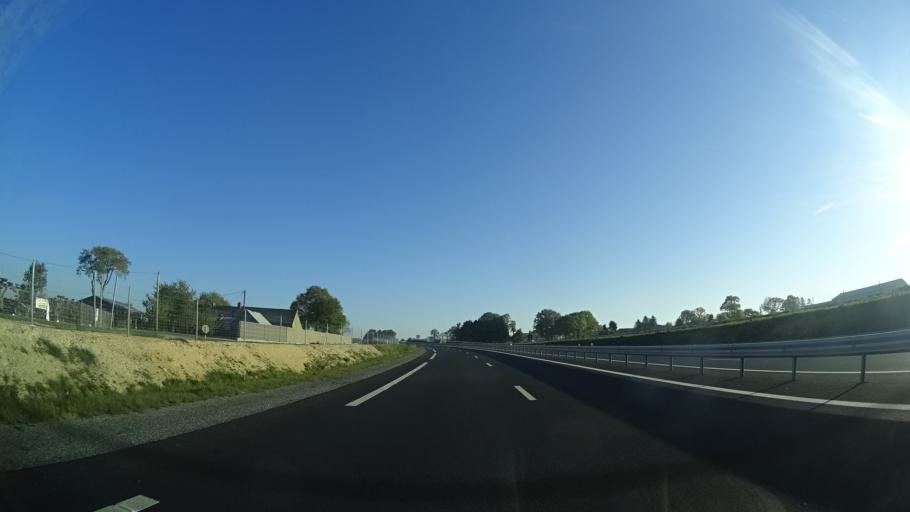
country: FR
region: Brittany
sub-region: Departement d'Ille-et-Vilaine
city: Pipriac
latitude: 47.8074
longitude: -1.9207
